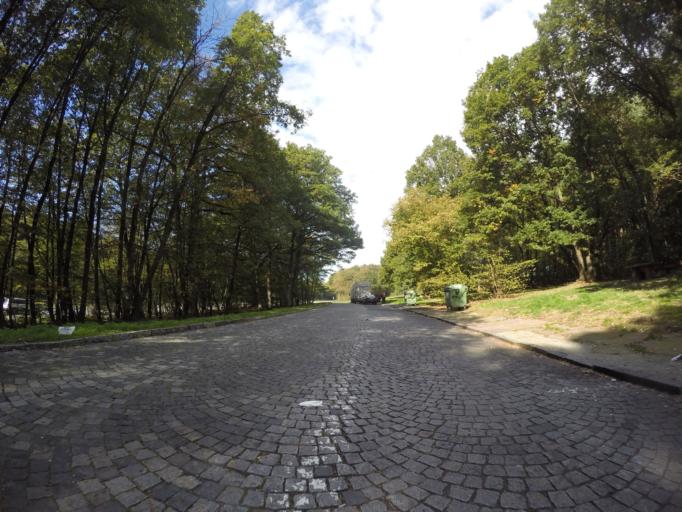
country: DE
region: Bavaria
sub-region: Regierungsbezirk Unterfranken
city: Bischbrunn
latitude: 49.8579
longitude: 9.4878
